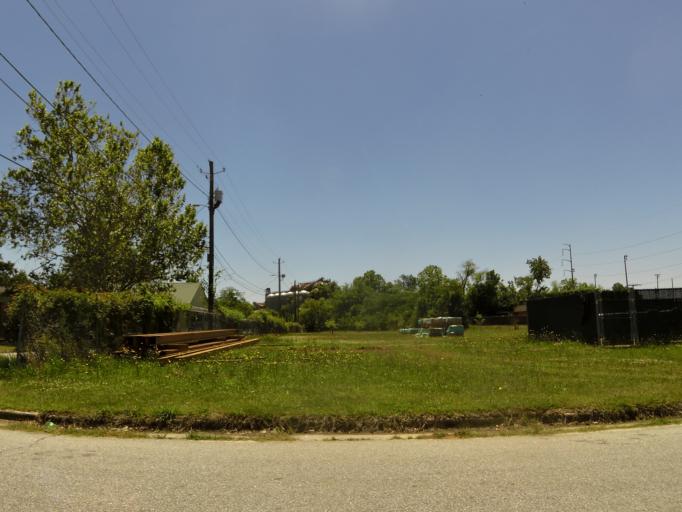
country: US
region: Georgia
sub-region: Richmond County
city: Augusta
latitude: 33.4668
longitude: -81.9685
